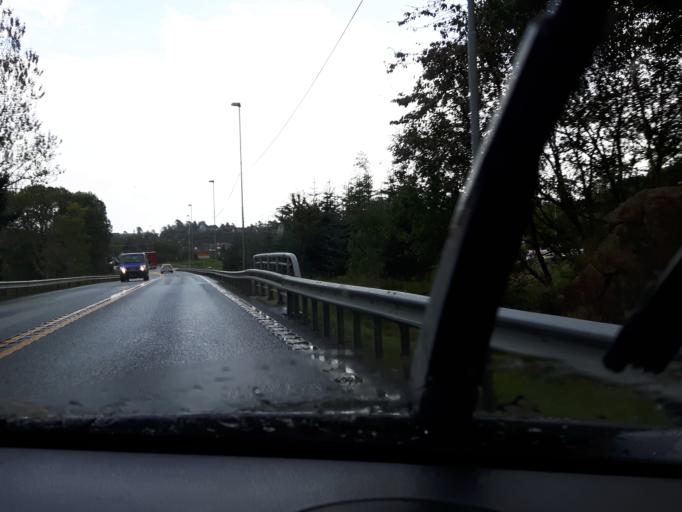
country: NO
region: Vest-Agder
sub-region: Sogne
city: Sogne
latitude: 58.0936
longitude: 7.7762
